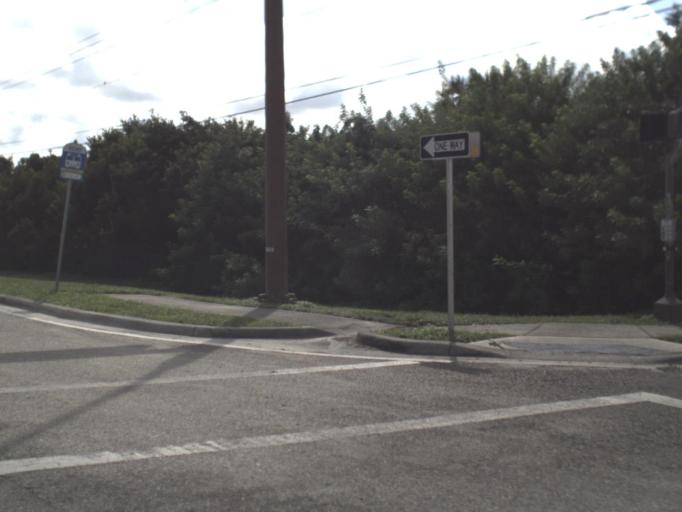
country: US
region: Florida
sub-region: Sarasota County
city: Plantation
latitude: 27.0495
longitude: -82.3584
